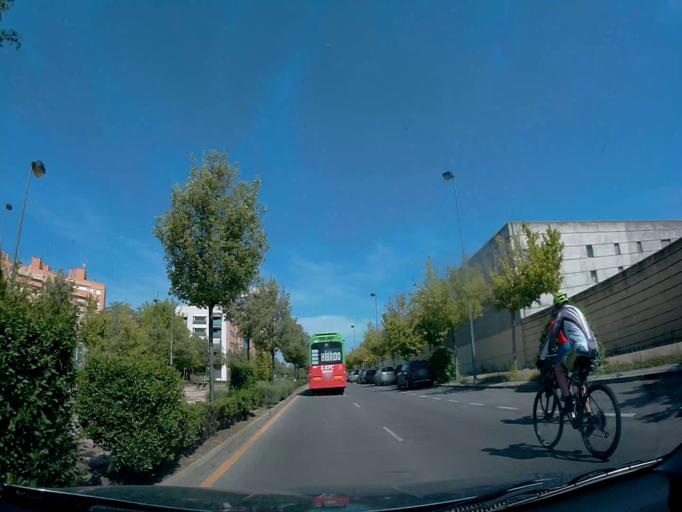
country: ES
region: Madrid
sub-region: Provincia de Madrid
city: Alcorcon
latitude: 40.3467
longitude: -3.8384
